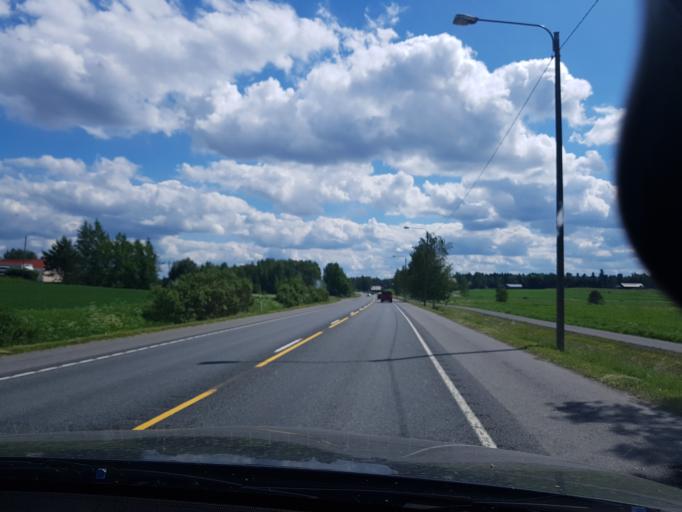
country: FI
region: Haeme
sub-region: Haemeenlinna
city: Parola
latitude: 61.0459
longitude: 24.3977
